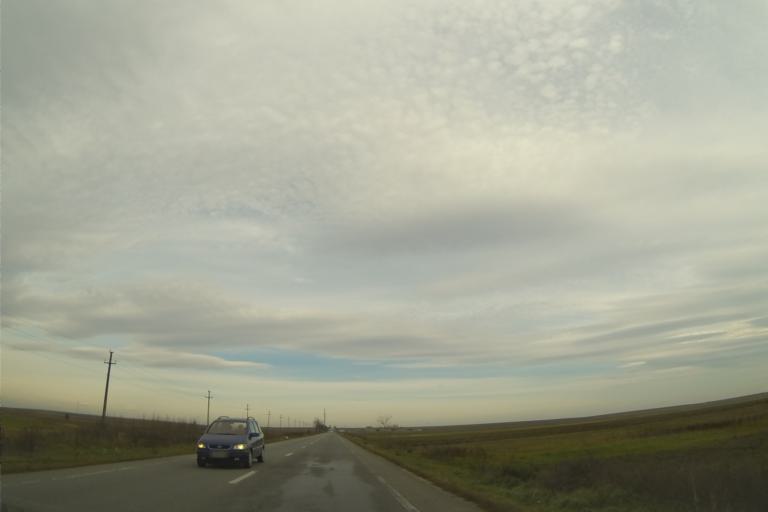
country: RO
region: Olt
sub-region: Comuna Valea Mare
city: Valea Mare
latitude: 44.4653
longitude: 24.4126
